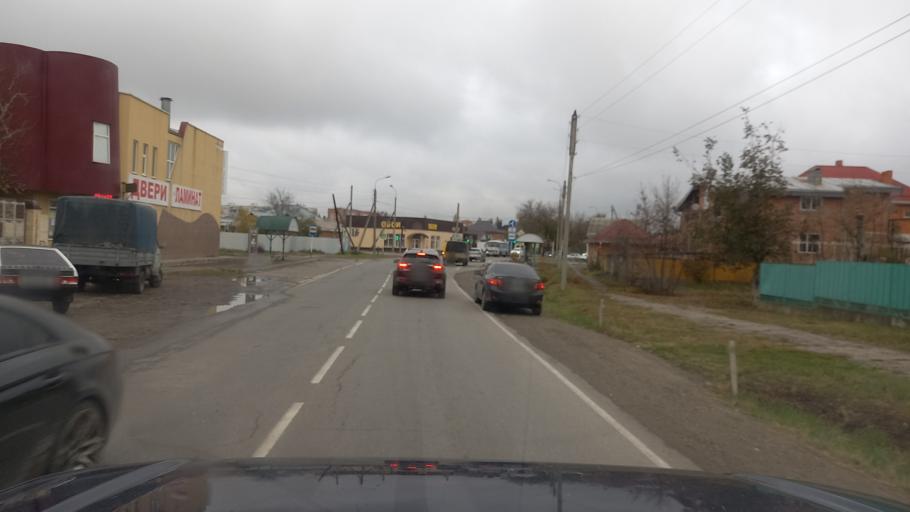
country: RU
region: Adygeya
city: Maykop
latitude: 44.6037
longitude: 40.0714
